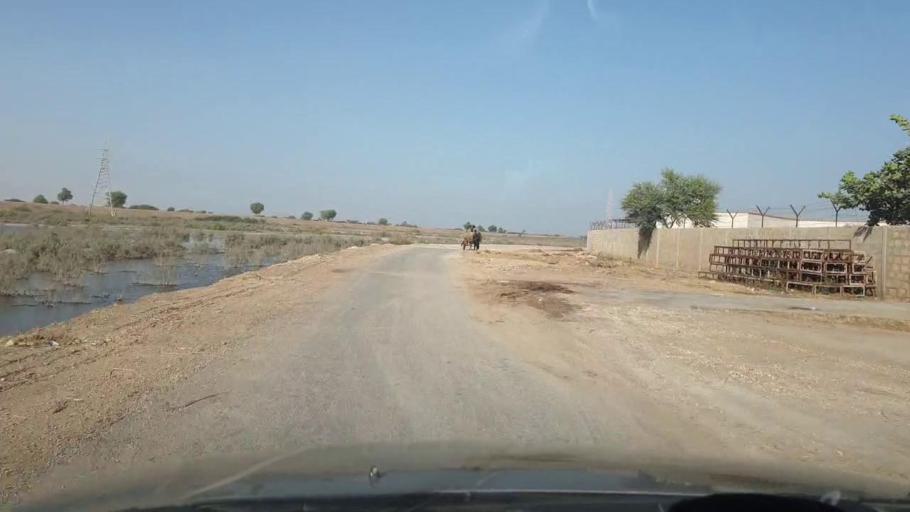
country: PK
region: Sindh
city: Bulri
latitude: 25.1057
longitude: 68.2391
